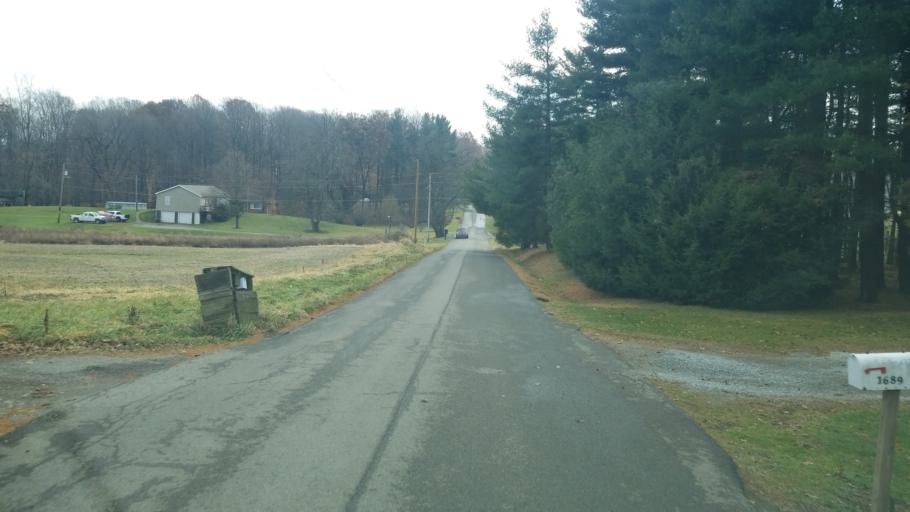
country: US
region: Ohio
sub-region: Richland County
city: Lincoln Heights
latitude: 40.8050
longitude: -82.4749
